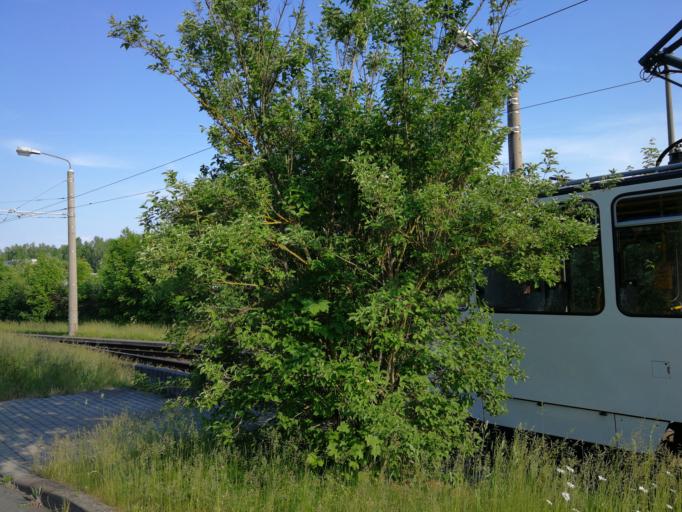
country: DE
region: Thuringia
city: Zedlitz
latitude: 50.8396
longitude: 12.0490
